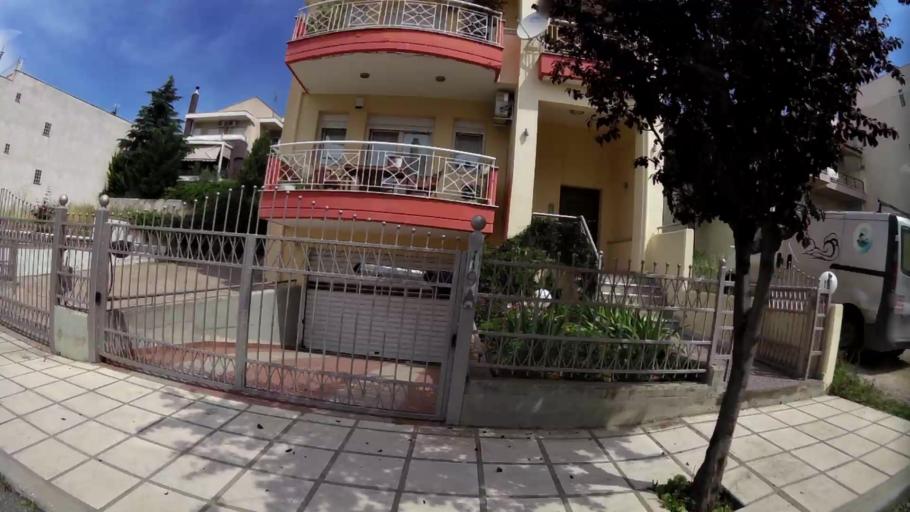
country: GR
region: Central Macedonia
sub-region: Nomos Thessalonikis
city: Pylaia
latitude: 40.5957
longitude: 22.9886
